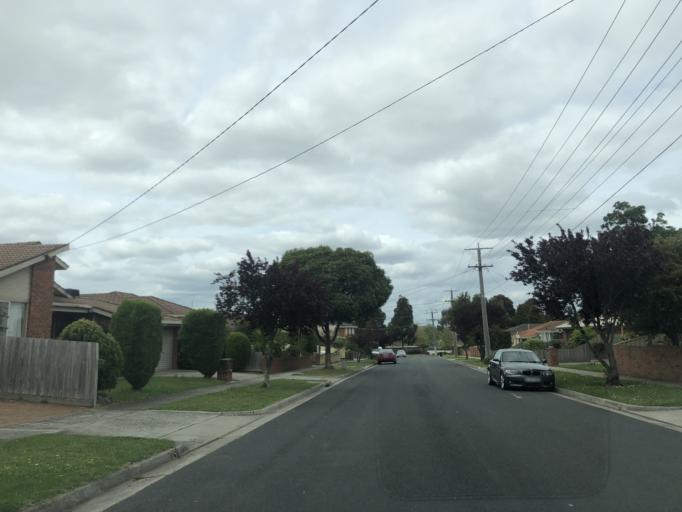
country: AU
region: Victoria
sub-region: Greater Dandenong
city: Dandenong North
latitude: -37.9532
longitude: 145.2174
